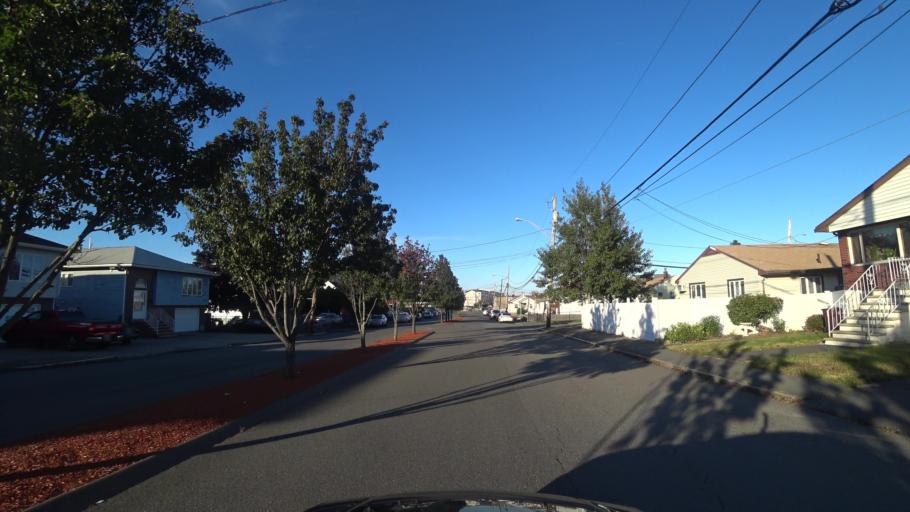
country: US
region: Massachusetts
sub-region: Suffolk County
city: Revere
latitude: 42.4214
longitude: -71.0097
